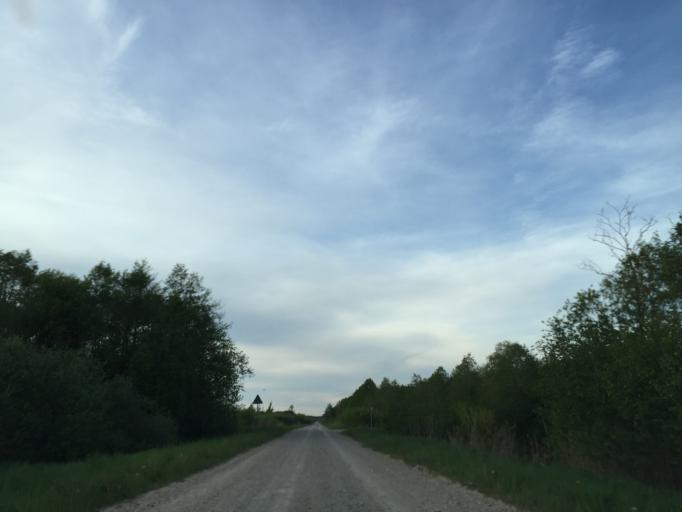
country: LV
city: Tireli
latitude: 56.7532
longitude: 23.5368
